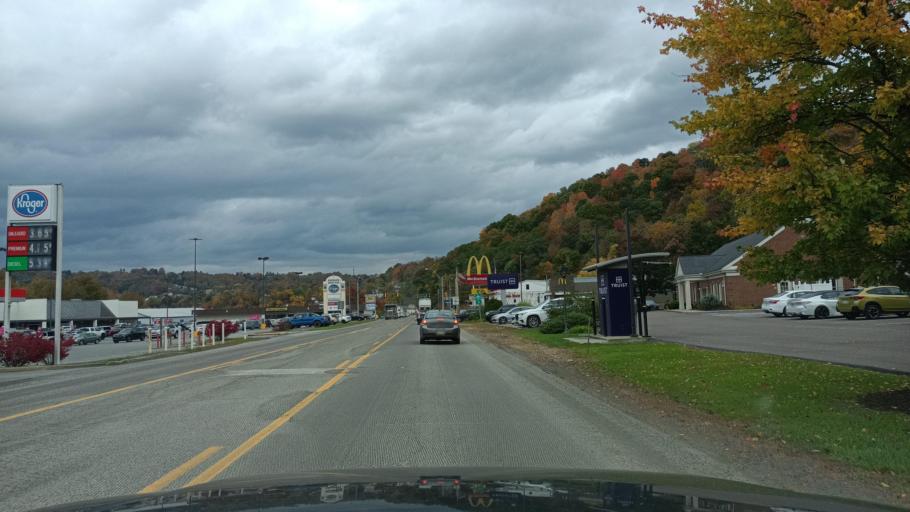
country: US
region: West Virginia
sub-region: Monongalia County
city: Brookhaven
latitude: 39.6211
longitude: -79.9233
